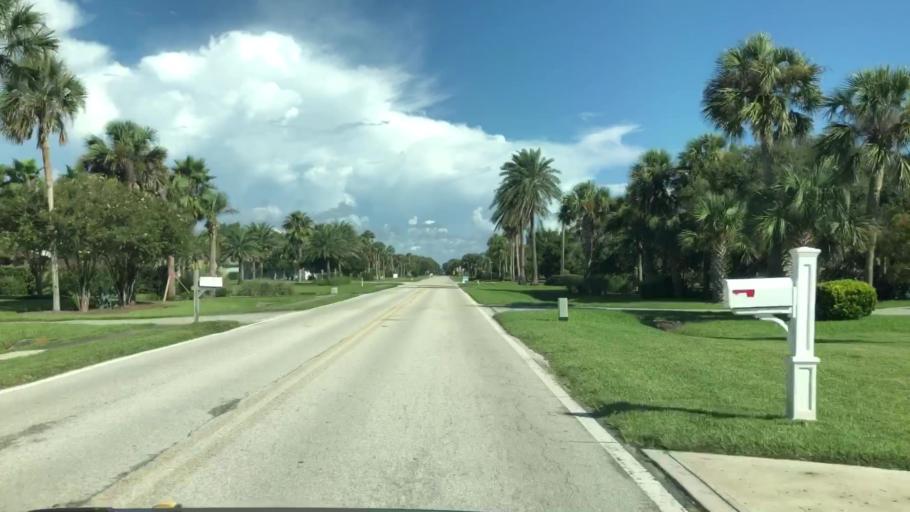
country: US
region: Florida
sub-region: Saint Johns County
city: Ponte Vedra Beach
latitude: 30.2571
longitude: -81.3842
